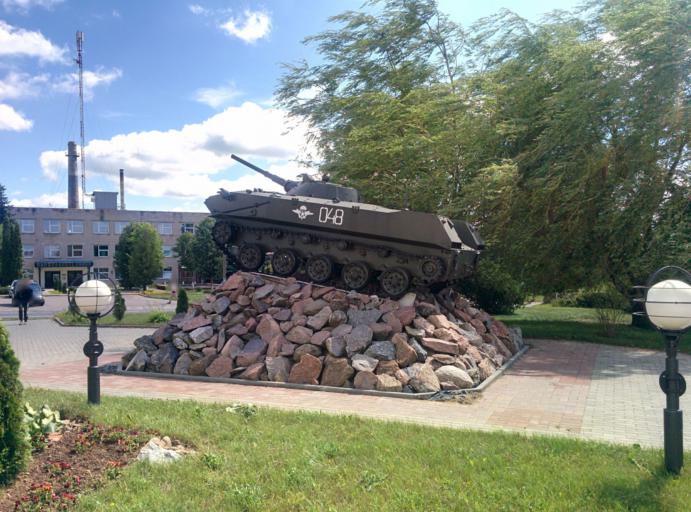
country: BY
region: Grodnenskaya
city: Ashmyany
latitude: 54.4271
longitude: 25.9265
